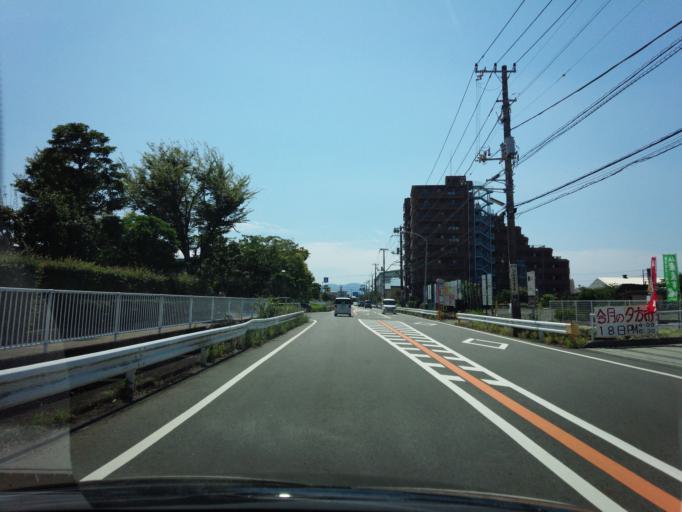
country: JP
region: Shizuoka
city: Numazu
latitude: 35.1208
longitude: 138.8341
